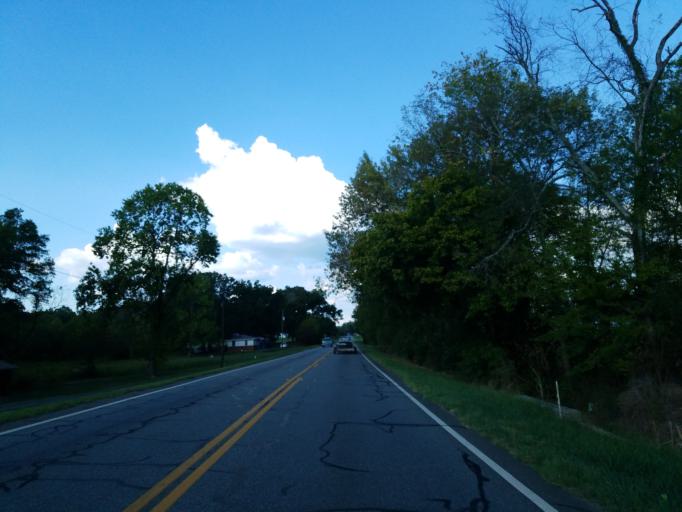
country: US
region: Georgia
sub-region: Murray County
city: Chatsworth
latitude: 34.5707
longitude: -84.7072
